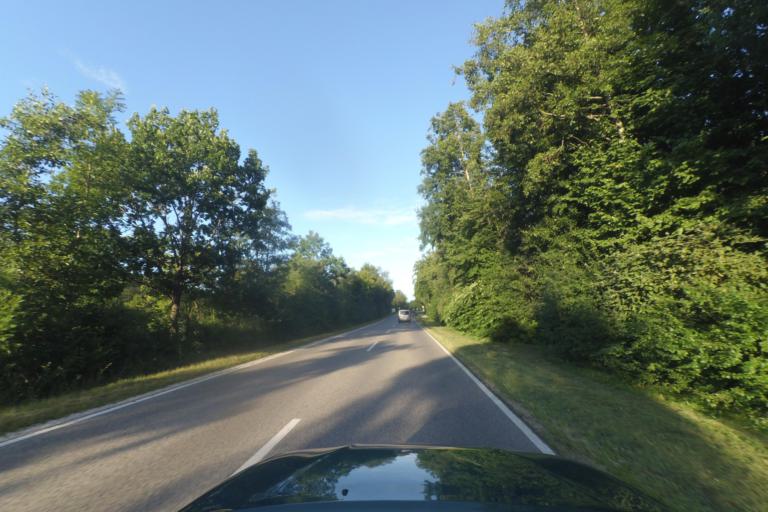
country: DE
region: Bavaria
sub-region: Upper Palatinate
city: Berching
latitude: 49.0399
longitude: 11.4803
